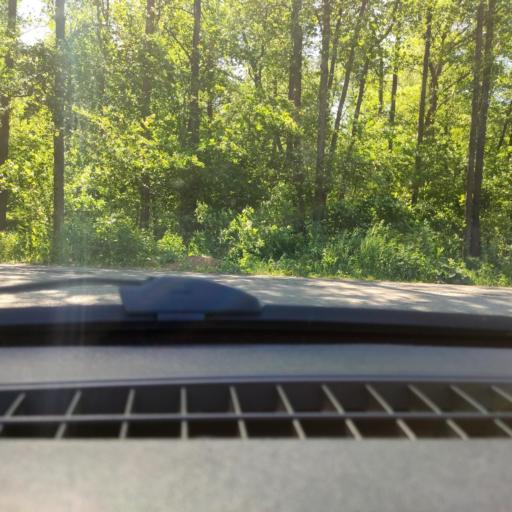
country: RU
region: Bashkortostan
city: Avdon
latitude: 54.6750
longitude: 55.8451
